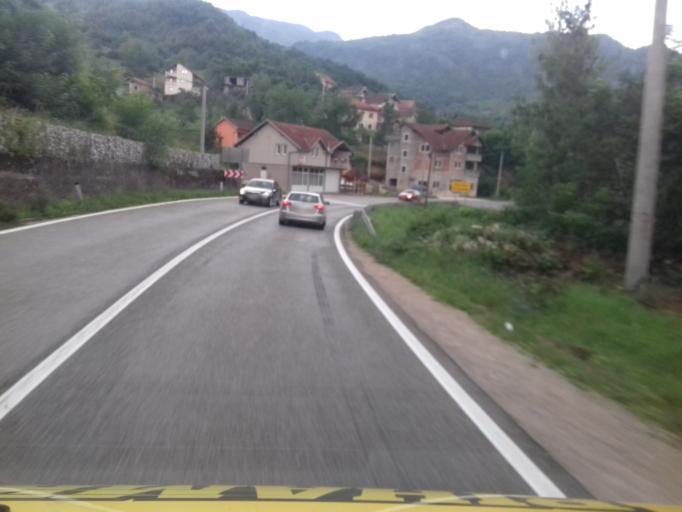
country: BA
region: Federation of Bosnia and Herzegovina
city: Jablanica
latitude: 43.6909
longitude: 17.8329
